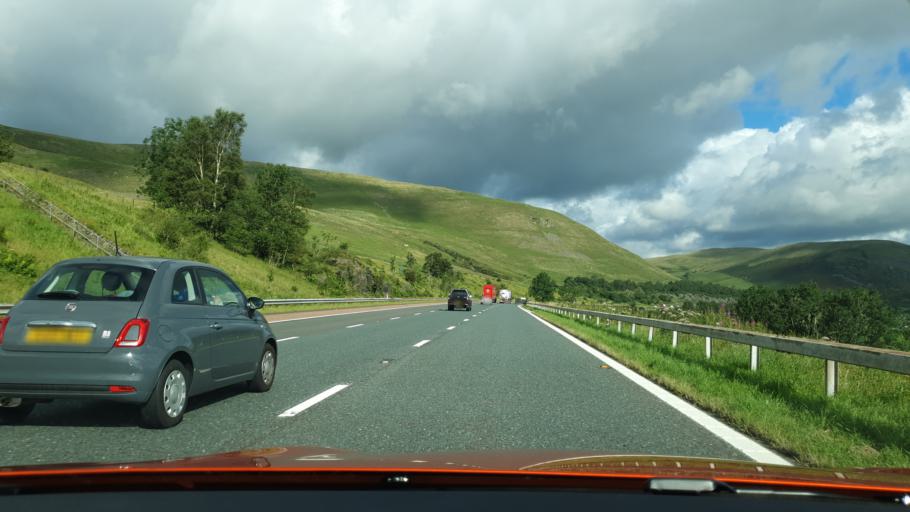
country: GB
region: England
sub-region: Cumbria
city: Sedbergh
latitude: 54.3941
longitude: -2.5976
